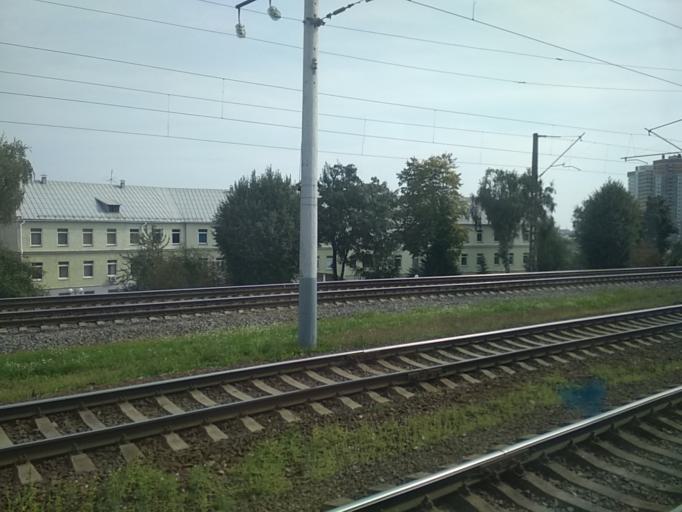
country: BY
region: Minsk
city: Minsk
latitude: 53.8863
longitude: 27.5622
